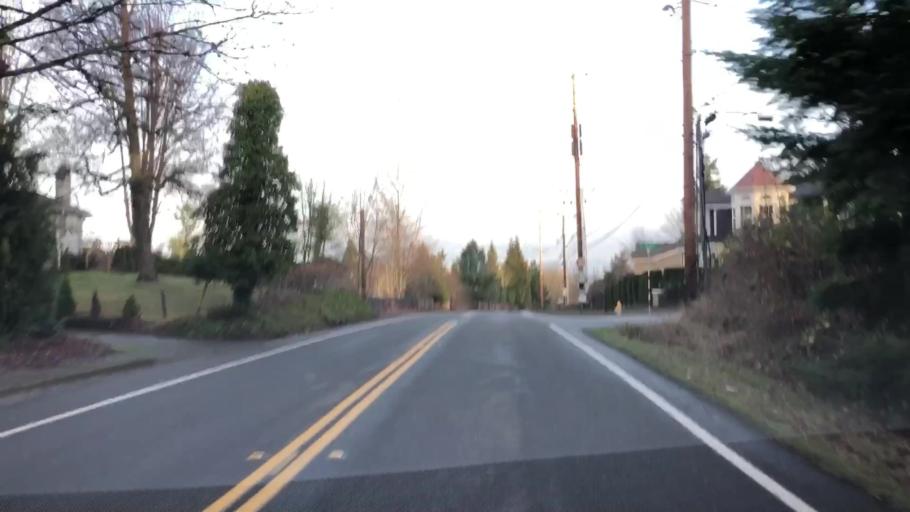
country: US
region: Washington
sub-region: King County
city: West Lake Sammamish
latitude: 47.5647
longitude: -122.1215
